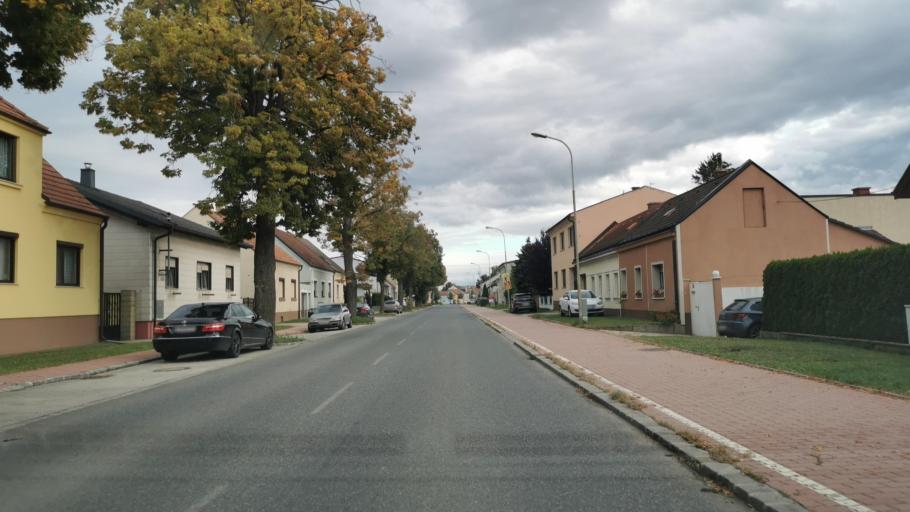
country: AT
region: Lower Austria
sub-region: Politischer Bezirk Ganserndorf
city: Obersiebenbrunn
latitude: 48.2593
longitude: 16.7018
